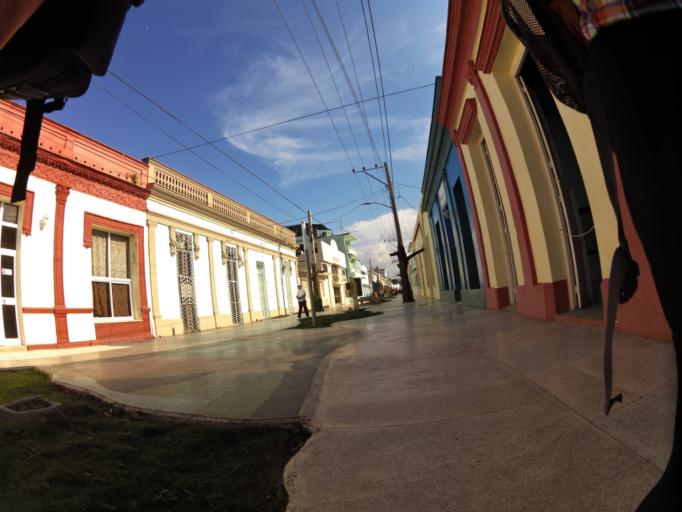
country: CU
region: Granma
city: Bayamo
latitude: 20.3697
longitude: -76.6466
